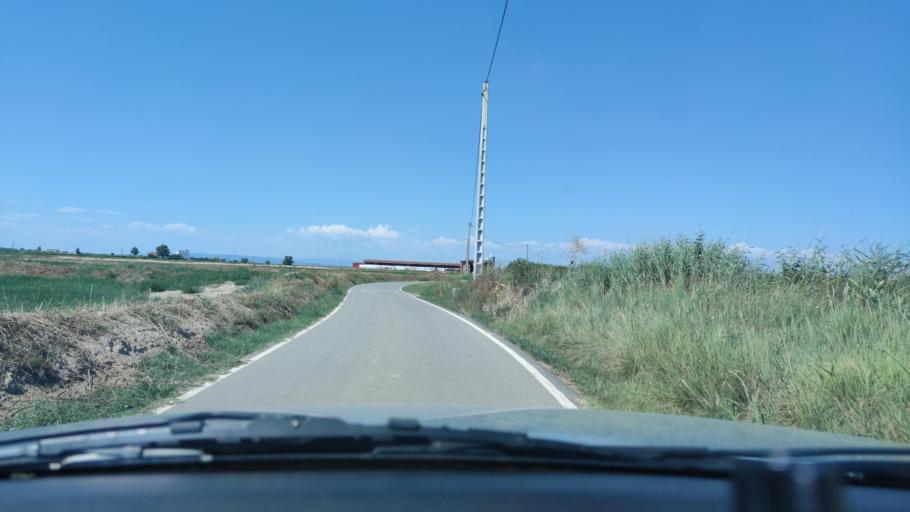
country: ES
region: Catalonia
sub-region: Provincia de Lleida
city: Torrefarrera
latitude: 41.6751
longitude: 0.6399
